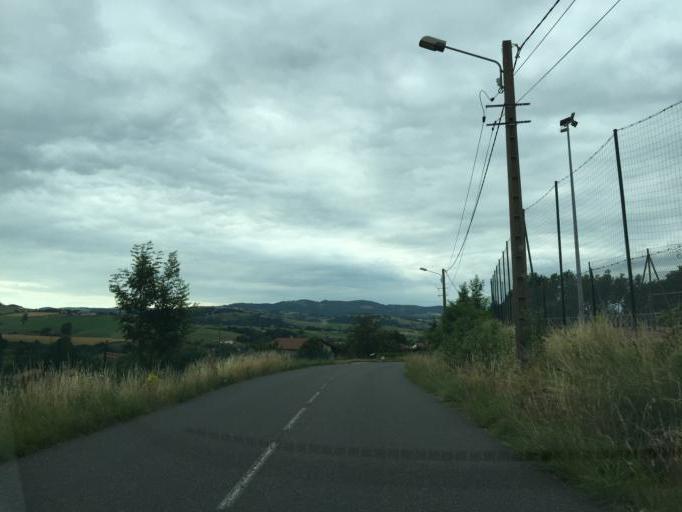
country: FR
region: Rhone-Alpes
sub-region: Departement de la Loire
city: Saint-Jean-Bonnefonds
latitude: 45.4484
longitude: 4.4808
